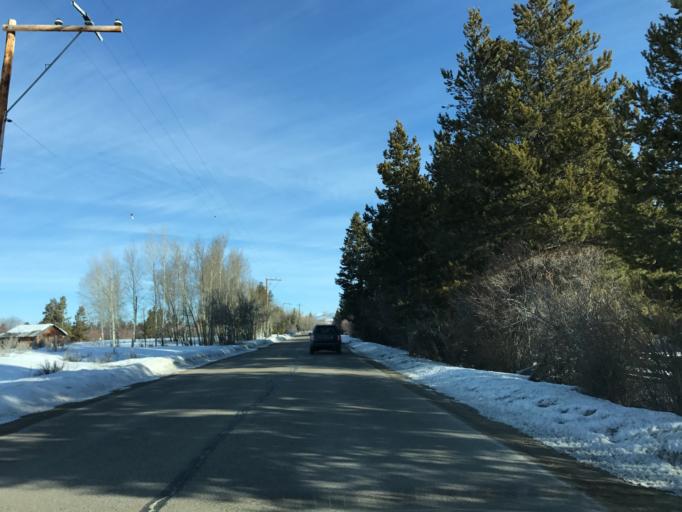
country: US
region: Wyoming
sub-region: Sublette County
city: Pinedale
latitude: 42.8581
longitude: -109.8612
